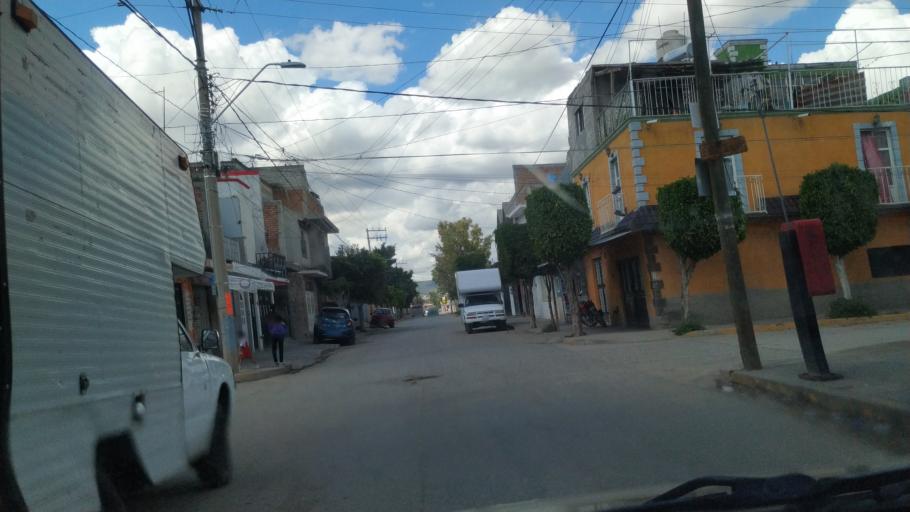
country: MX
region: Guanajuato
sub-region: Leon
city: Medina
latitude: 21.1452
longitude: -101.6288
